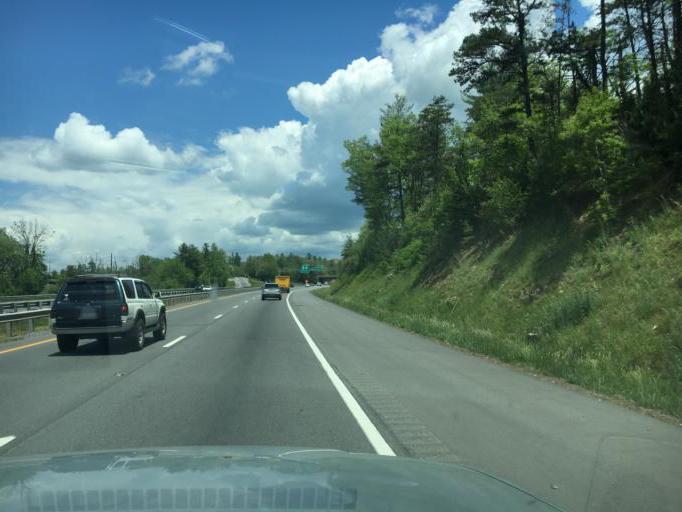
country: US
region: North Carolina
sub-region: Buncombe County
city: Weaverville
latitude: 35.7004
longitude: -82.5756
